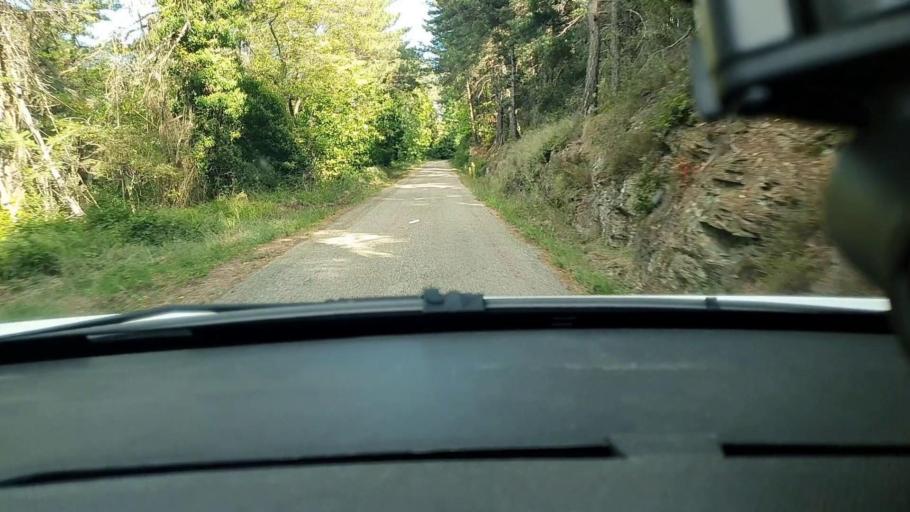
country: FR
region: Languedoc-Roussillon
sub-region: Departement du Gard
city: Besseges
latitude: 44.3820
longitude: 3.9919
